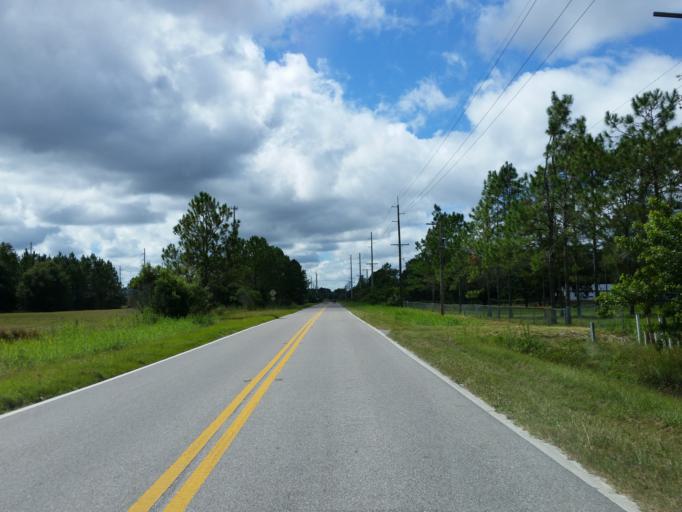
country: US
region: Florida
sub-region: Pasco County
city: Zephyrhills West
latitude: 28.1745
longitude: -82.2557
